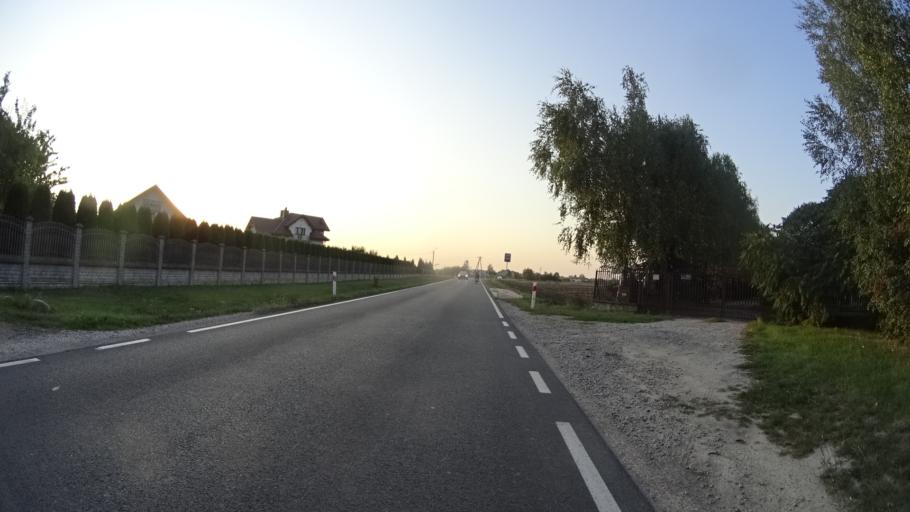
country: PL
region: Masovian Voivodeship
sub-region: Powiat warszawski zachodni
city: Ozarow Mazowiecki
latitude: 52.2397
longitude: 20.7523
